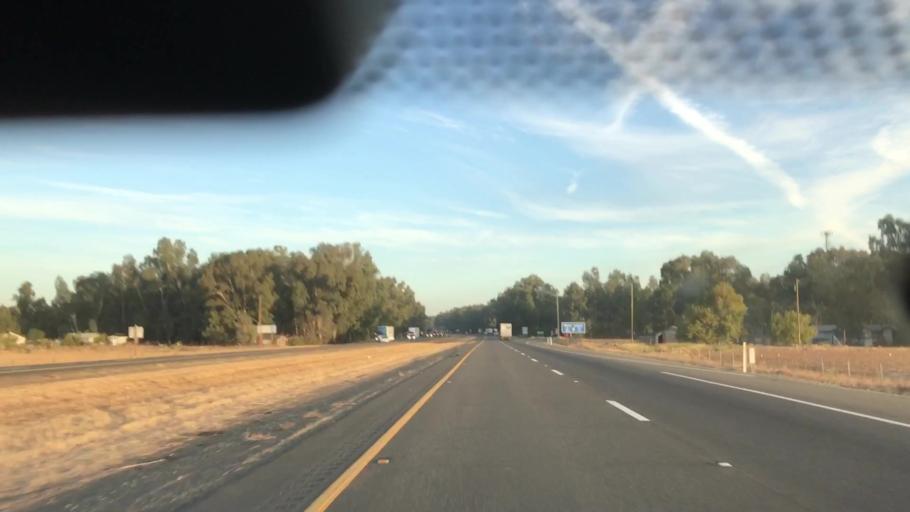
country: US
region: California
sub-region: Yolo County
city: Dunnigan
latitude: 38.8883
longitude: -121.9765
